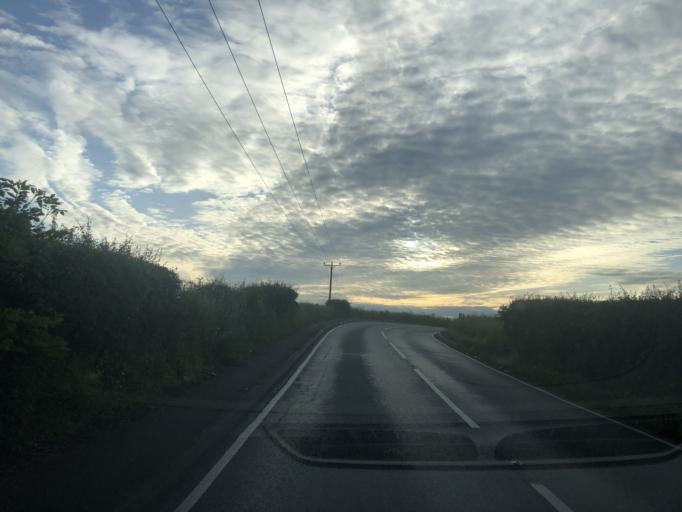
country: GB
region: Scotland
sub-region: Fife
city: Buckhaven
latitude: 56.1798
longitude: -3.0527
